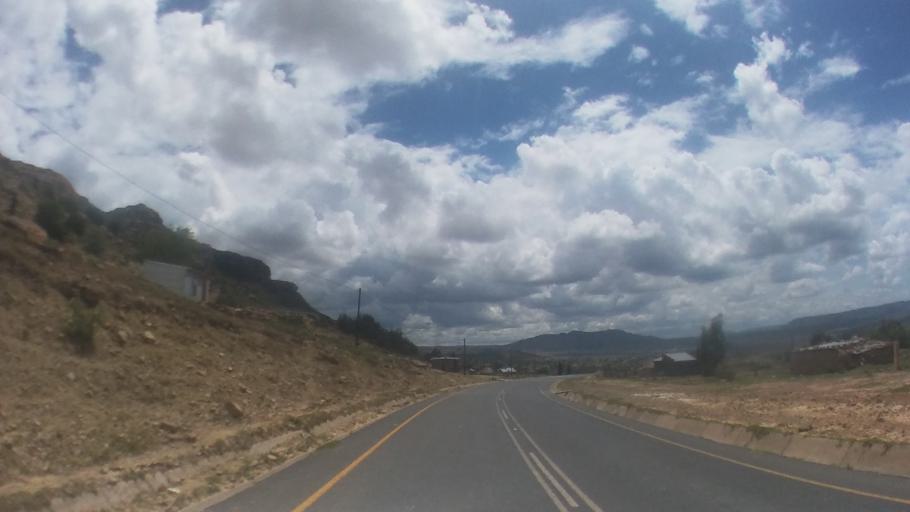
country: LS
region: Maseru
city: Maseru
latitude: -29.4271
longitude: 27.4693
